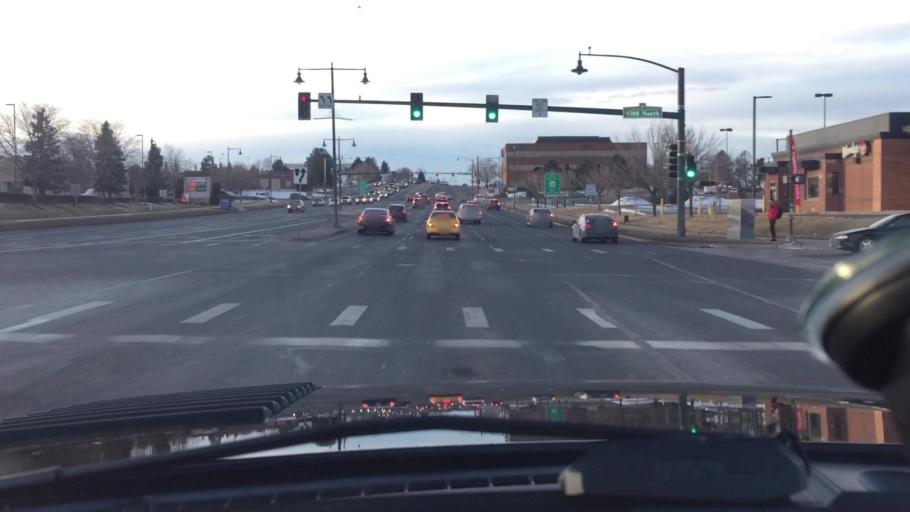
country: US
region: Colorado
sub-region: Adams County
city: Westminster
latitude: 39.8656
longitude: -105.0533
